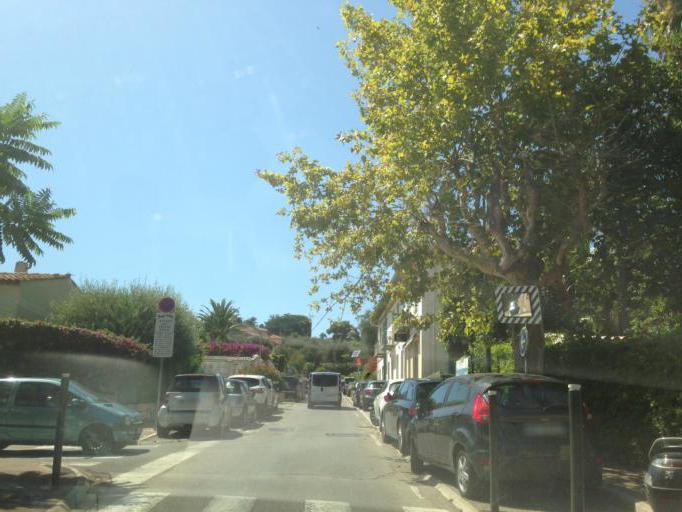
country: FR
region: Provence-Alpes-Cote d'Azur
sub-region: Departement des Alpes-Maritimes
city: Saint-Jean-Cap-Ferrat
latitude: 43.6920
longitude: 7.3321
